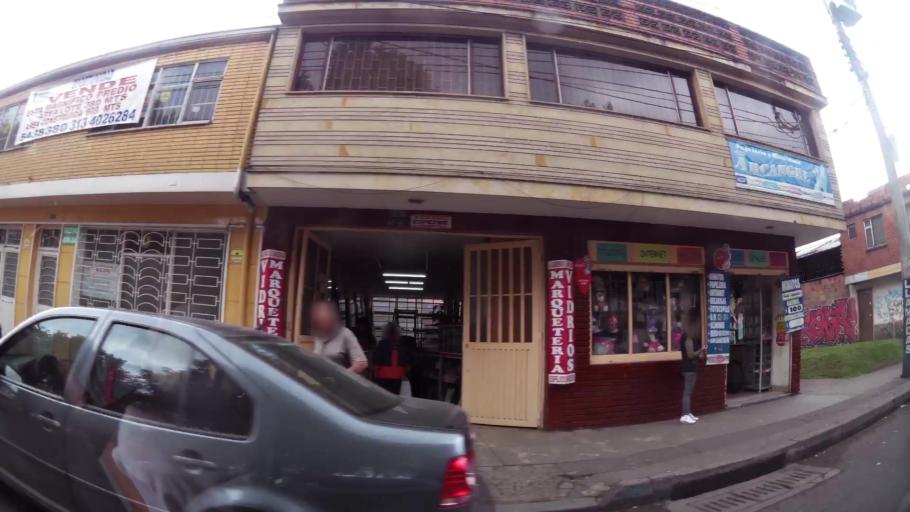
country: CO
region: Bogota D.C.
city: Bogota
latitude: 4.6739
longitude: -74.0975
